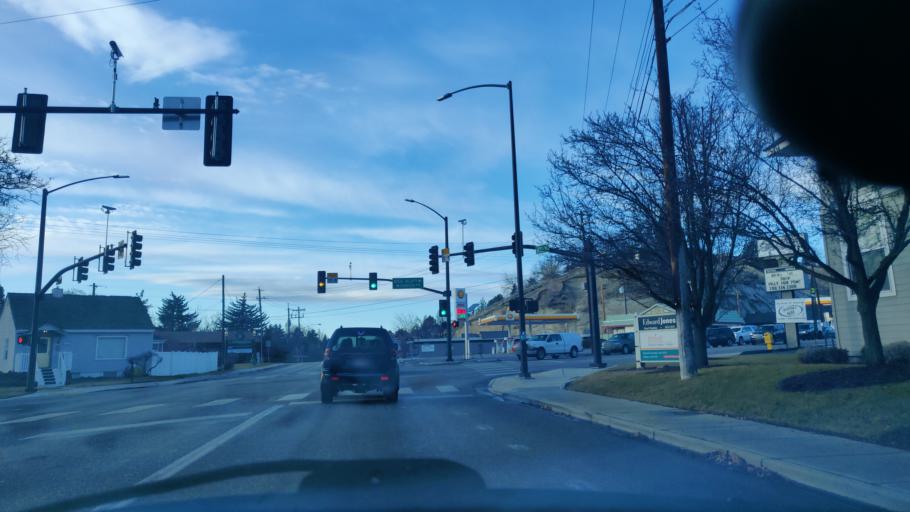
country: US
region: Idaho
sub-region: Ada County
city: Boise
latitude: 43.6401
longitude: -116.2080
